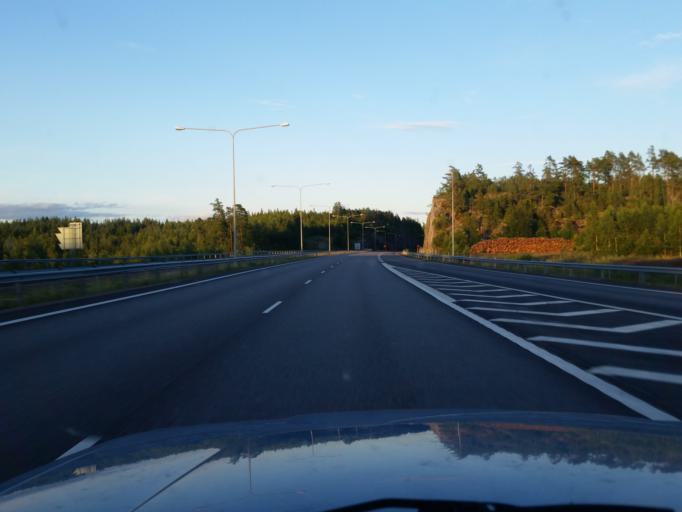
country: FI
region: Varsinais-Suomi
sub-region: Turku
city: Paimio
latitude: 60.4276
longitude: 22.7290
